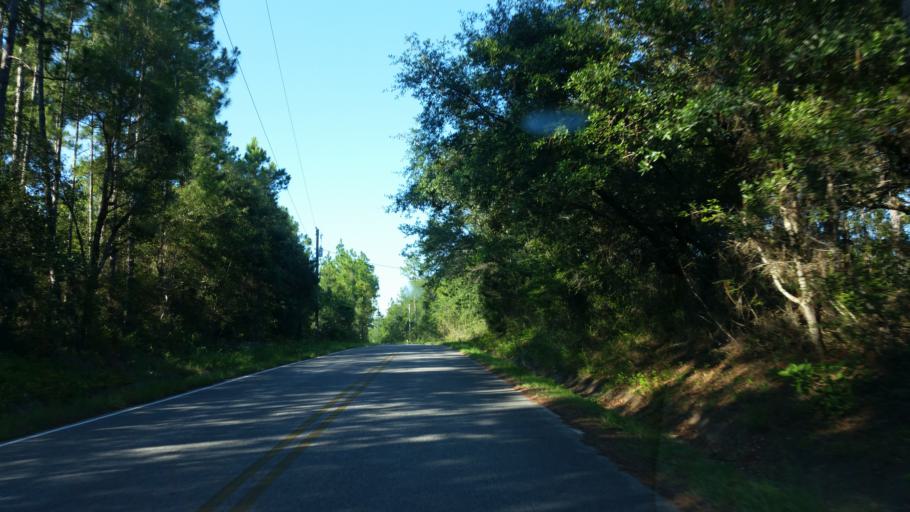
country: US
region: Florida
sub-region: Escambia County
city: Bellview
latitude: 30.4883
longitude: -87.3870
